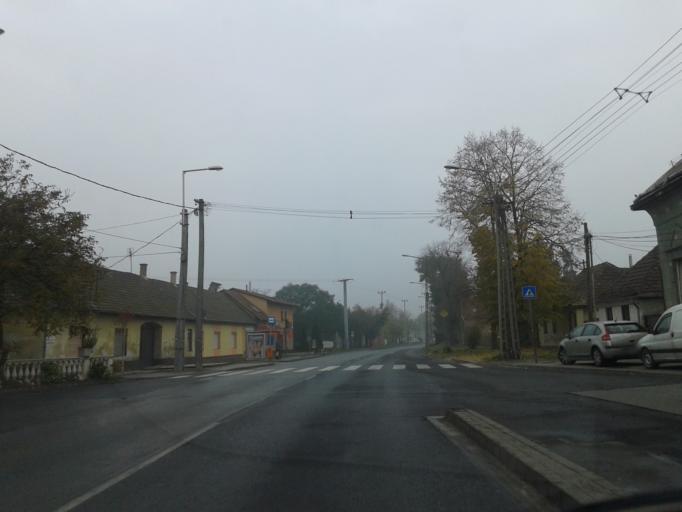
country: HU
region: Pest
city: Halasztelek
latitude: 47.3910
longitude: 18.9815
